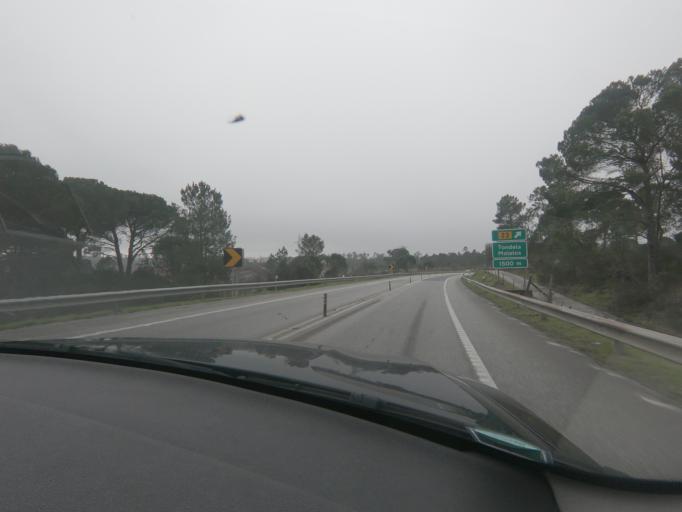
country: PT
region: Viseu
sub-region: Concelho de Tondela
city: Tondela
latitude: 40.5283
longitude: -8.0691
